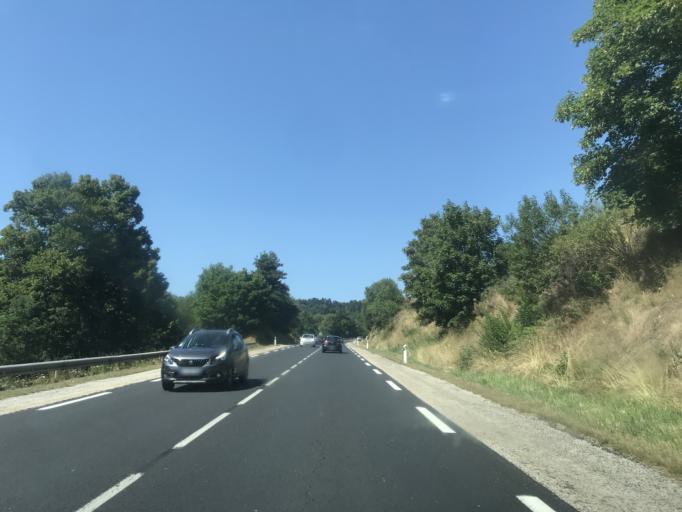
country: FR
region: Auvergne
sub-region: Departement de la Haute-Loire
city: Allegre
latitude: 45.1239
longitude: 3.7071
